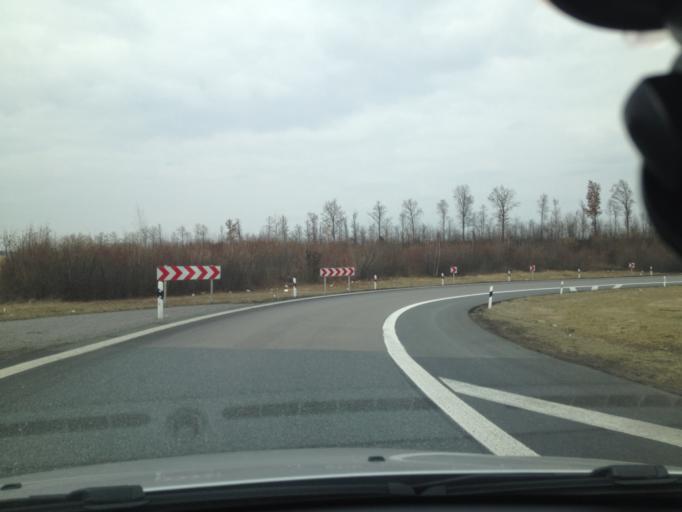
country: DE
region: Bavaria
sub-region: Regierungsbezirk Unterfranken
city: Biebelried
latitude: 49.7804
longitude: 10.0909
